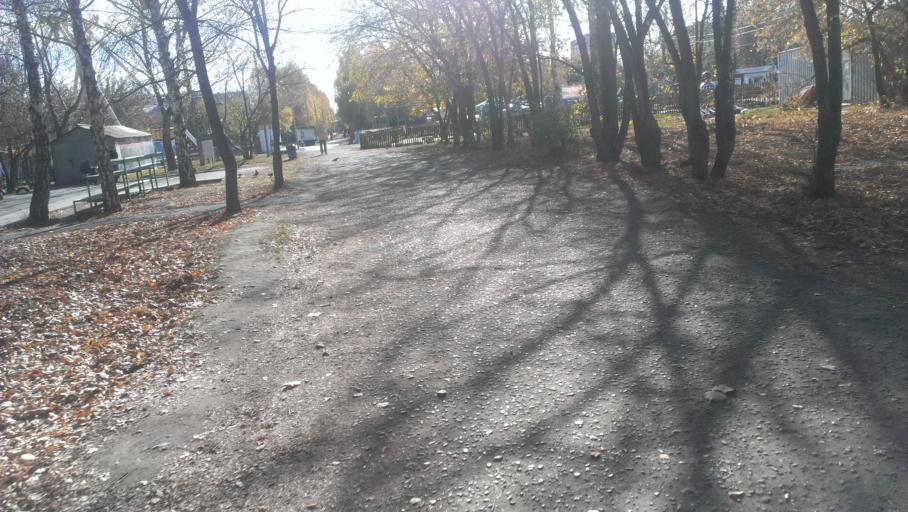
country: RU
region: Altai Krai
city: Novosilikatnyy
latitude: 53.3587
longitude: 83.6849
